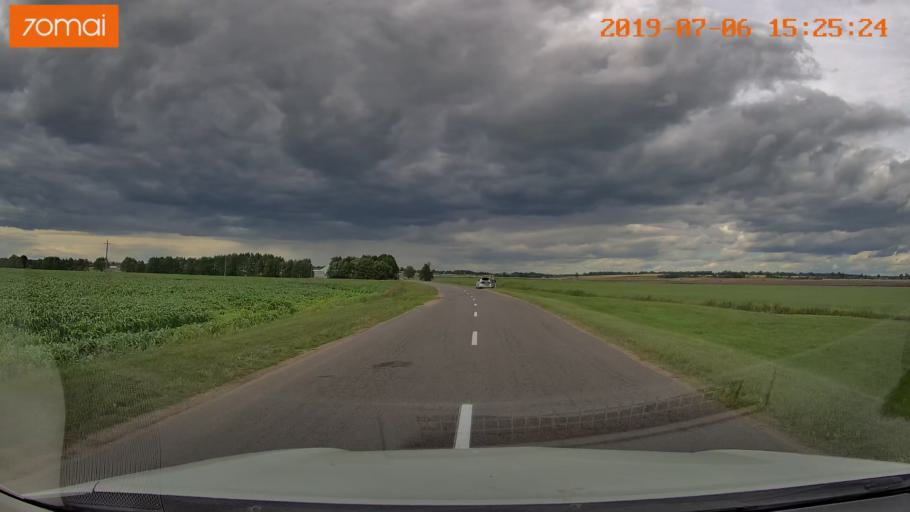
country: BY
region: Minsk
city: Valozhyn
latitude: 54.0313
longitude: 26.6044
